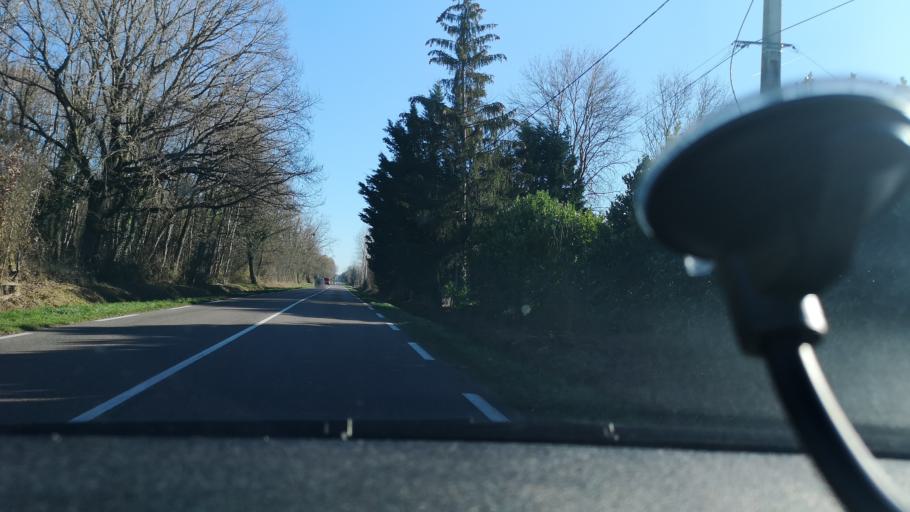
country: FR
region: Bourgogne
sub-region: Departement de Saone-et-Loire
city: Saint-Marcel
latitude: 46.7821
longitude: 4.9367
